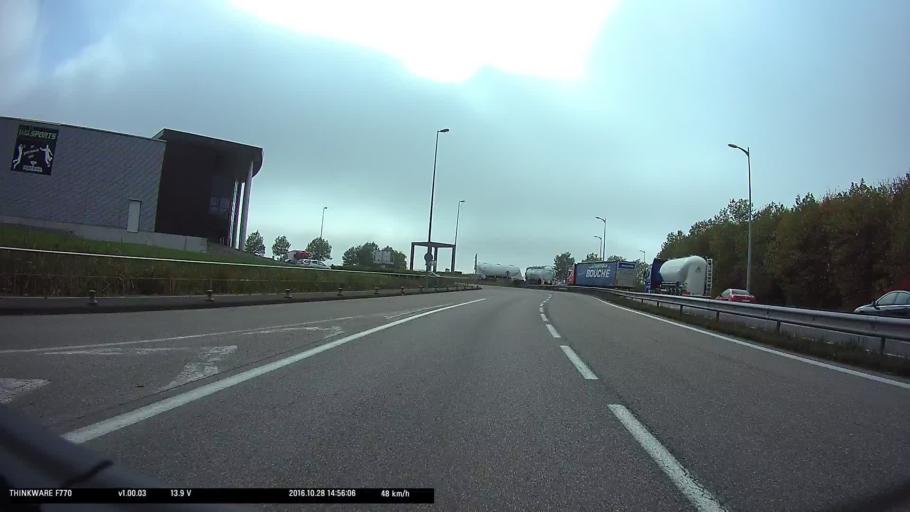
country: FR
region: Lorraine
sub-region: Departement de la Moselle
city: Phalsbourg
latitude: 48.7700
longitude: 7.2393
